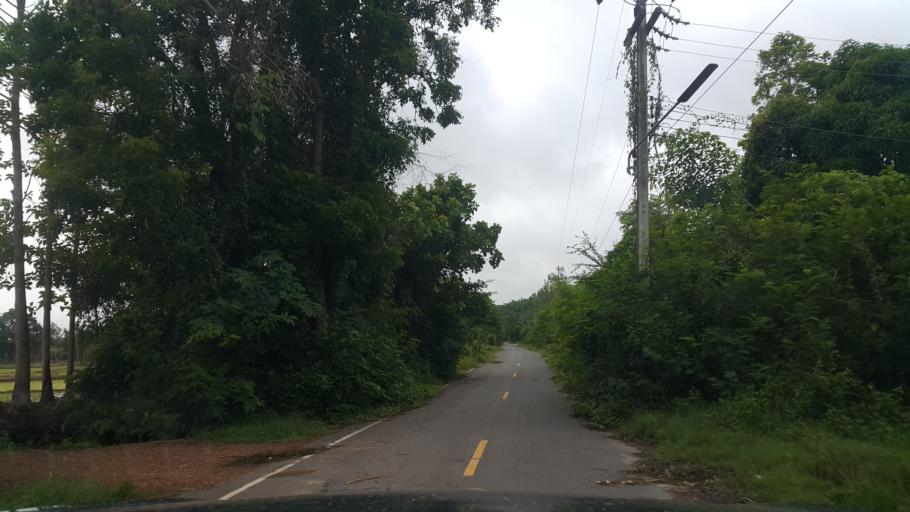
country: TH
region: Sukhothai
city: Sawankhalok
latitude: 17.3068
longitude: 99.7087
